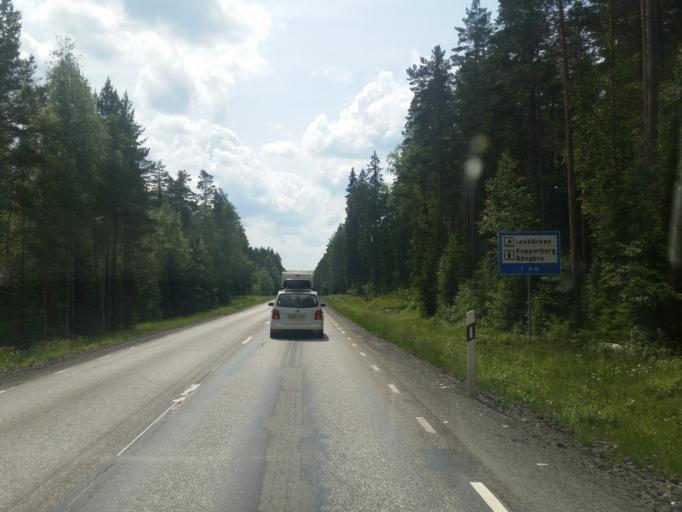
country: SE
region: OErebro
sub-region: Ljusnarsbergs Kommun
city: Kopparberg
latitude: 59.9103
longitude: 15.0220
